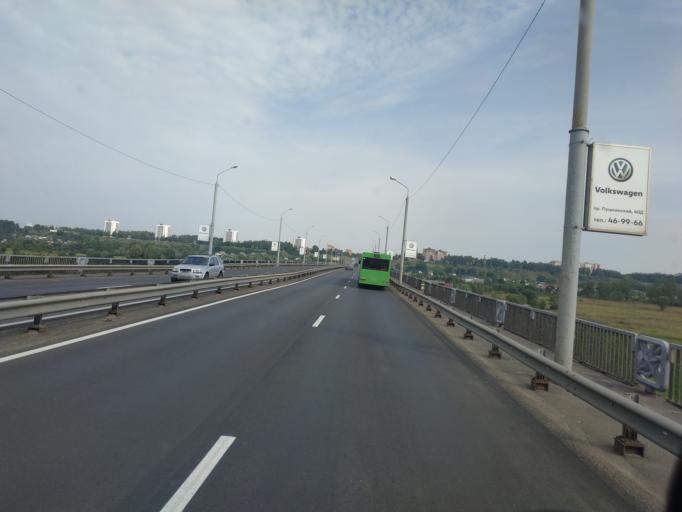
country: BY
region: Mogilev
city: Mahilyow
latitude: 53.8912
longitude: 30.3753
